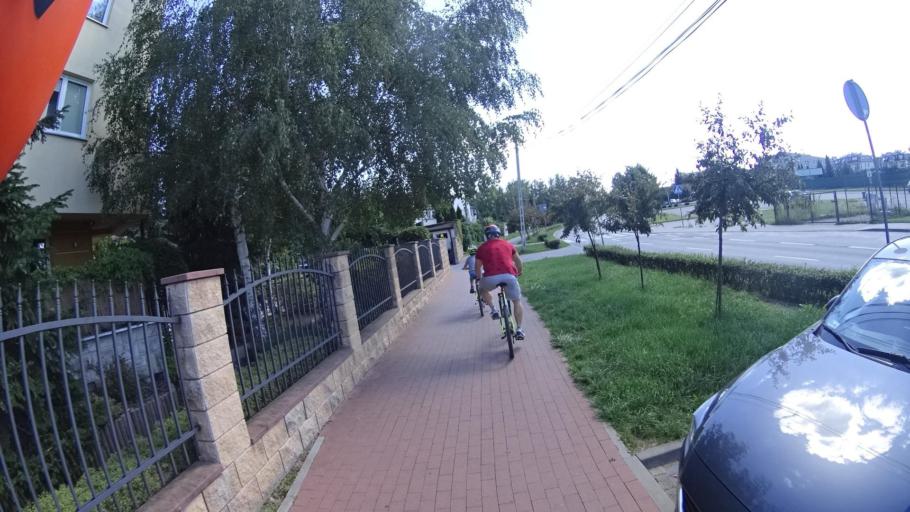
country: PL
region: Masovian Voivodeship
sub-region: Powiat piaseczynski
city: Jozefoslaw
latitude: 52.0983
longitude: 21.0535
